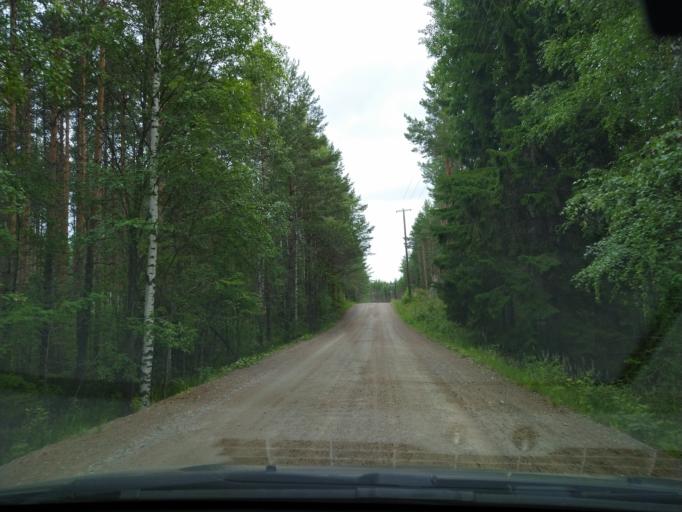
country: FI
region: Southern Savonia
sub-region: Mikkeli
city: Maentyharju
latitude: 61.1389
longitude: 26.8876
